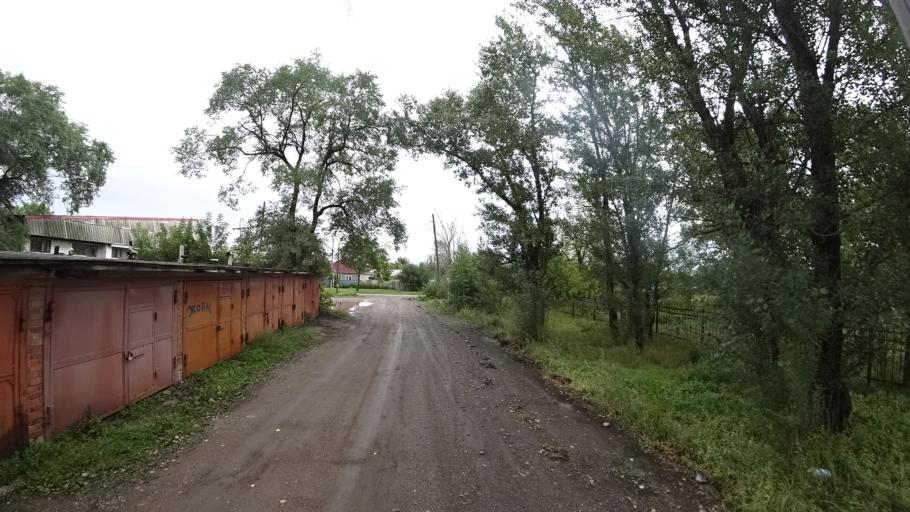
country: RU
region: Primorskiy
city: Chernigovka
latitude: 44.3420
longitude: 132.5810
